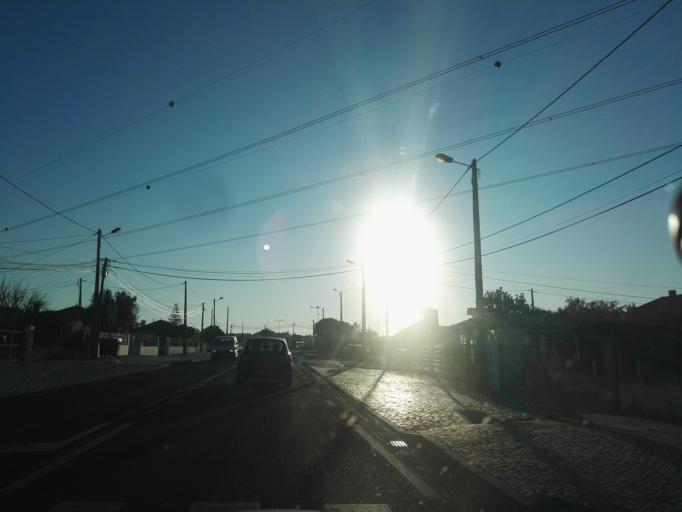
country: PT
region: Santarem
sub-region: Benavente
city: Samora Correia
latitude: 38.9272
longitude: -8.8803
